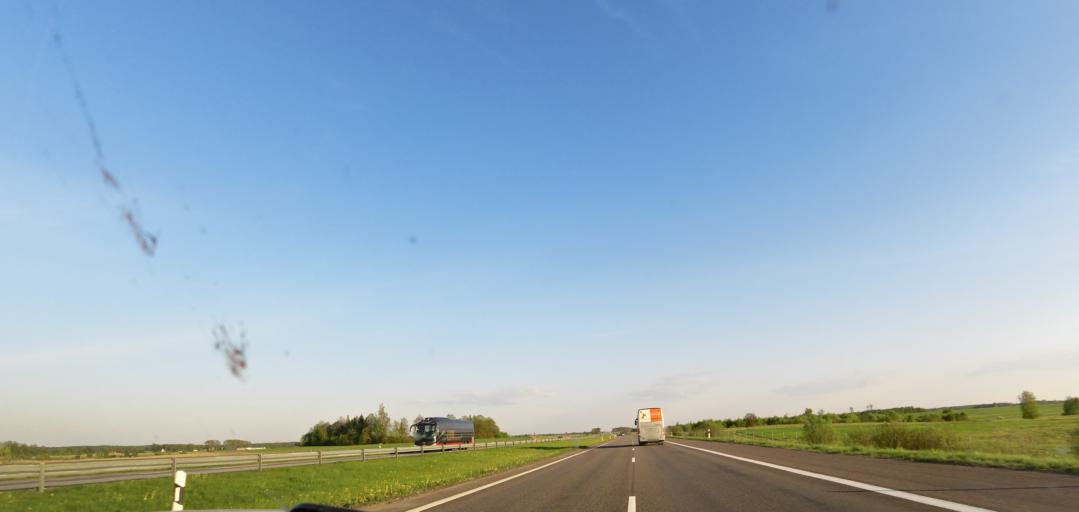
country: LT
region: Vilnius County
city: Ukmerge
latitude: 55.1520
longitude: 24.8232
